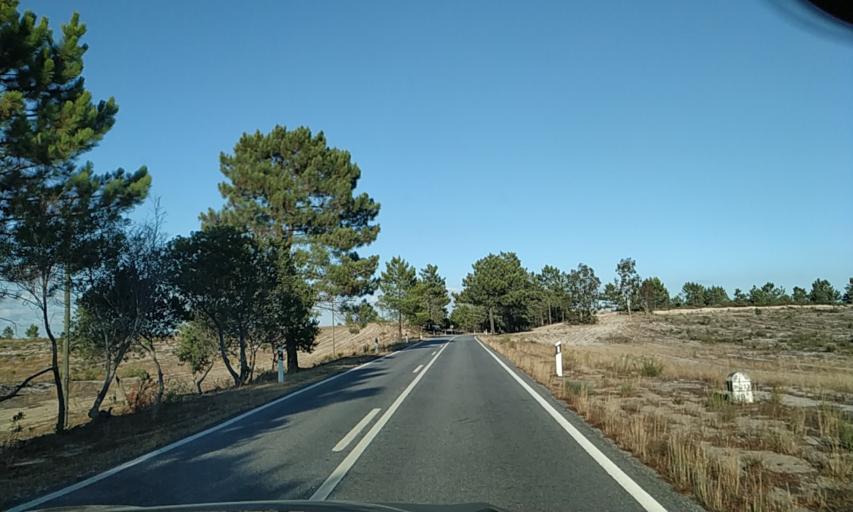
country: PT
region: Setubal
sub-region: Alcacer do Sal
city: Alcacer do Sal
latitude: 38.4066
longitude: -8.6971
